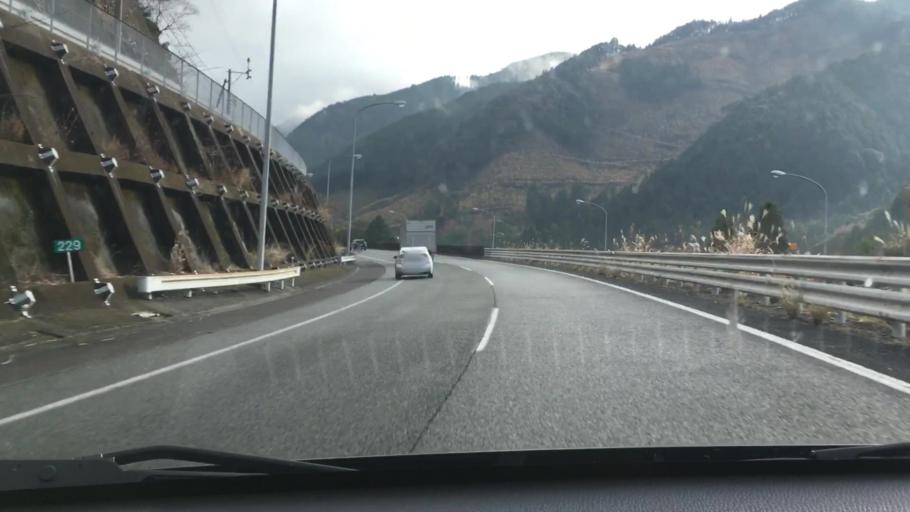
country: JP
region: Kumamoto
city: Yatsushiro
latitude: 32.4033
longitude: 130.6977
